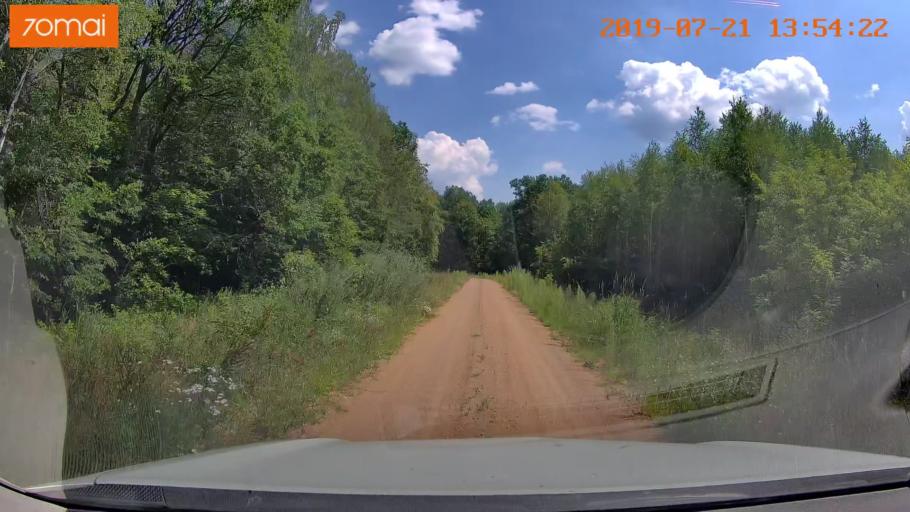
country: BY
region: Grodnenskaya
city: Lyubcha
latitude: 53.7763
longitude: 26.0727
